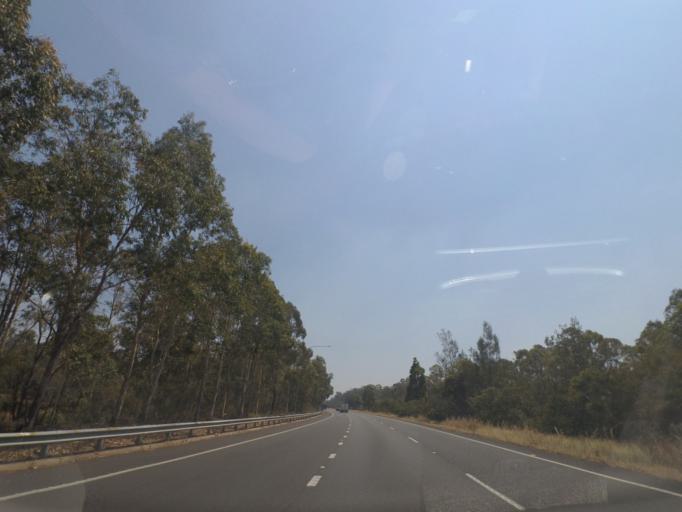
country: AU
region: New South Wales
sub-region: Newcastle
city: Beresfield
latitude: -32.8346
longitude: 151.6350
